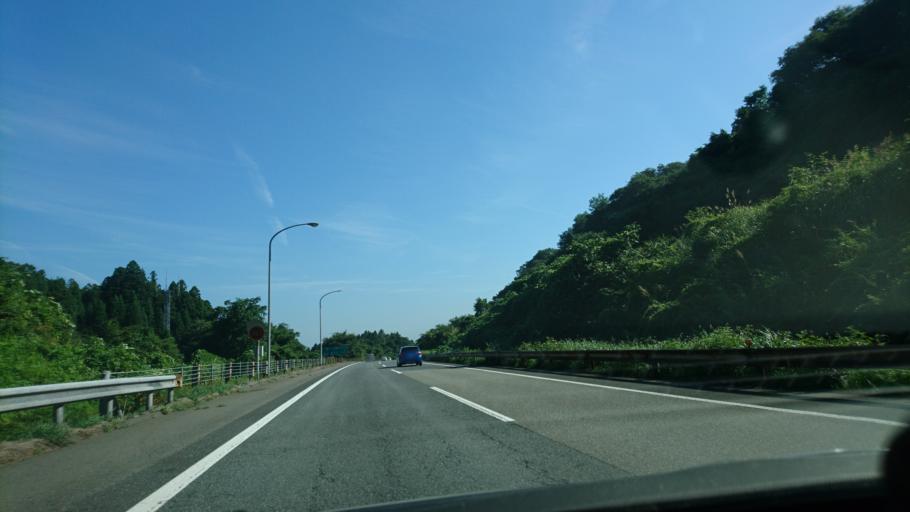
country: JP
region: Iwate
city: Ichinoseki
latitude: 38.9568
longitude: 141.1072
